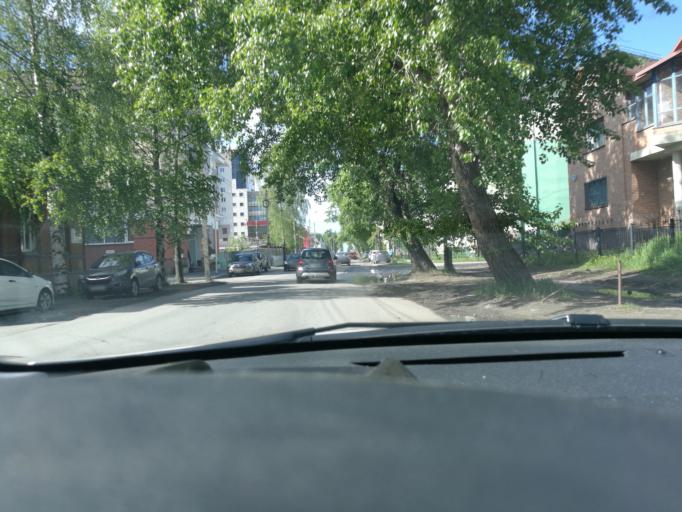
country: RU
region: Arkhangelskaya
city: Arkhangel'sk
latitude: 64.5382
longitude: 40.5308
